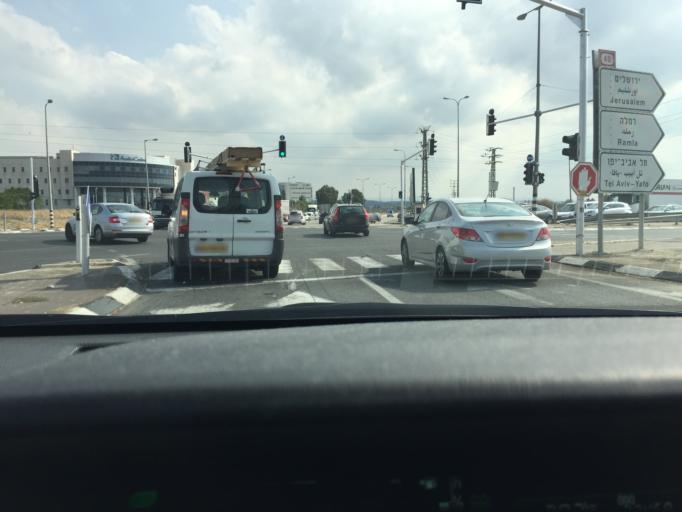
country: IL
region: Central District
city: Lod
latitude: 31.9897
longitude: 34.9063
